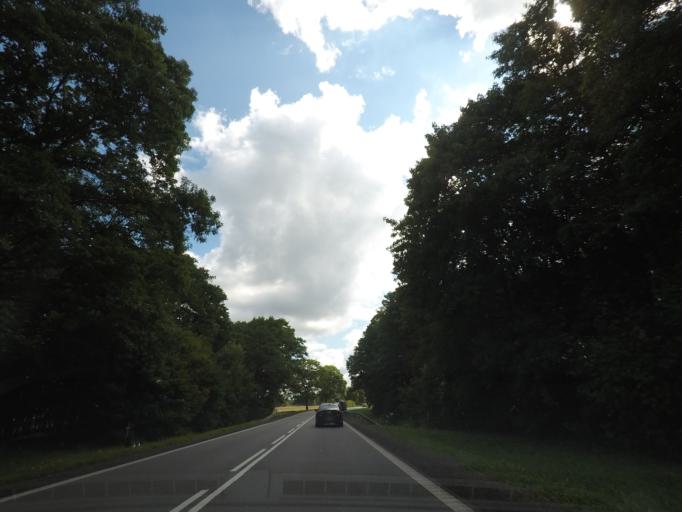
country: PL
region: Pomeranian Voivodeship
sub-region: Powiat wejherowski
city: Leczyce
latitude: 54.5716
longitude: 17.9492
